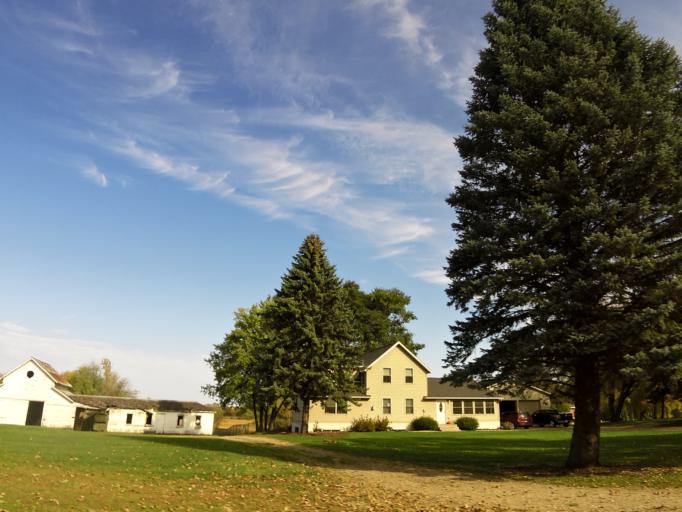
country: US
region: Minnesota
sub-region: Scott County
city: Prior Lake
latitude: 44.6888
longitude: -93.4400
